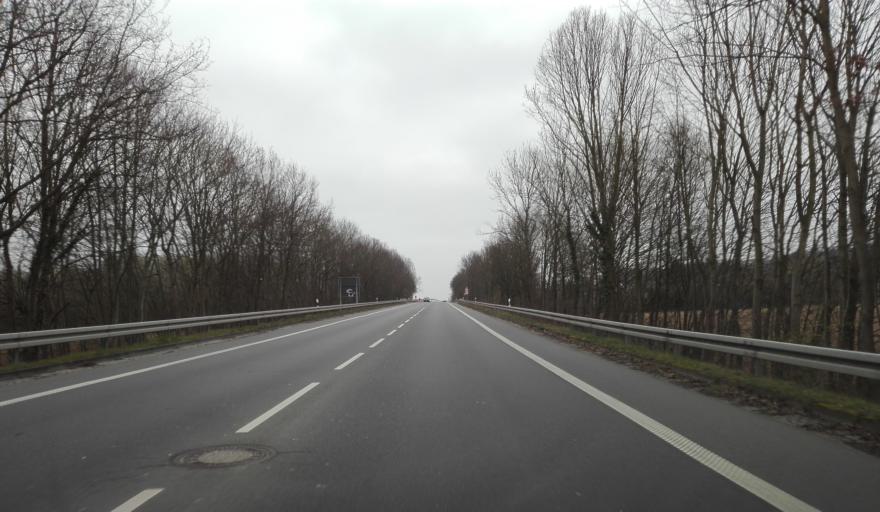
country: DE
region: Hesse
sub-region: Regierungsbezirk Darmstadt
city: Rossdorf
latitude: 49.8618
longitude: 8.7705
